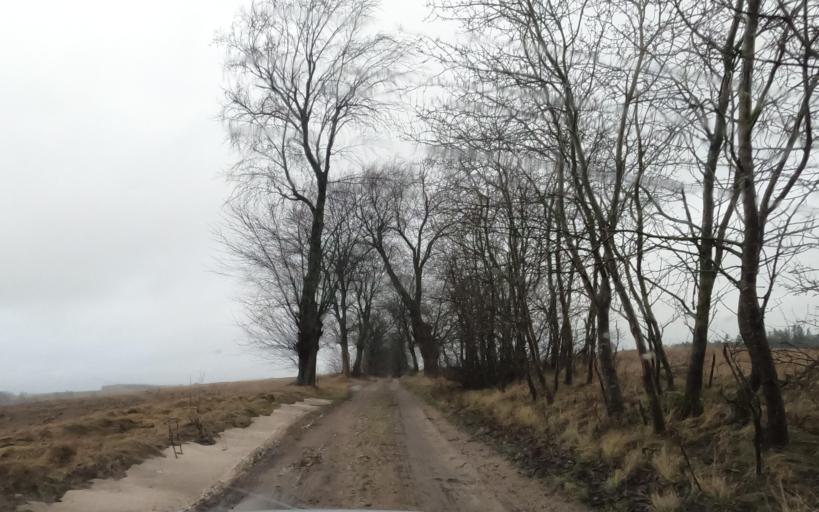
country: PL
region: West Pomeranian Voivodeship
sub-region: Powiat szczecinecki
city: Szczecinek
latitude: 53.6228
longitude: 16.6743
